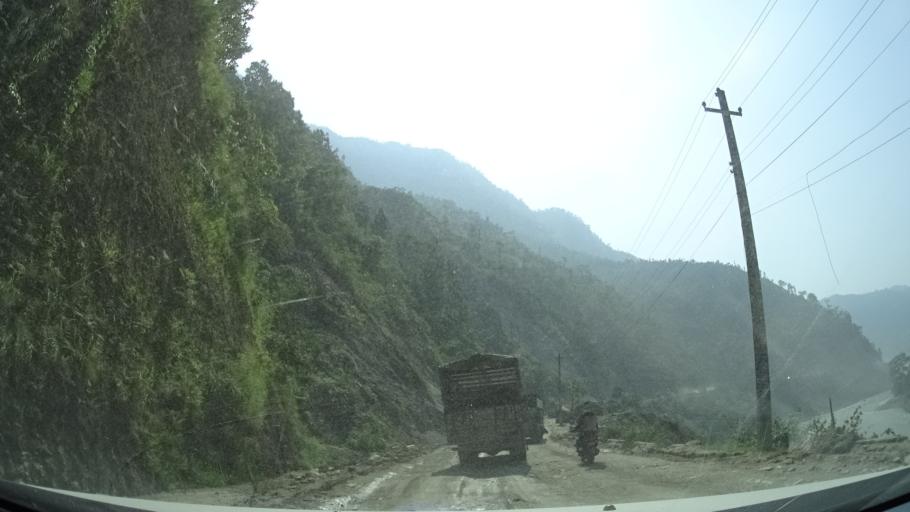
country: NP
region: Central Region
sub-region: Narayani Zone
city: Bharatpur
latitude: 27.8318
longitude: 84.5505
